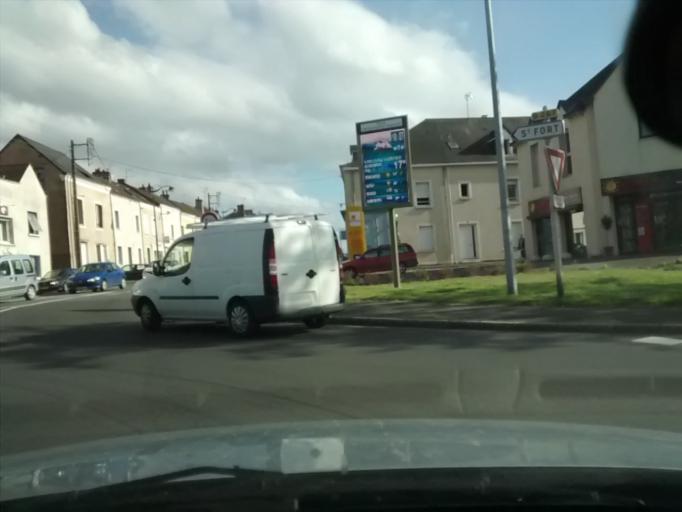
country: FR
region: Pays de la Loire
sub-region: Departement de la Mayenne
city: Chateau-Gontier
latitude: 47.8232
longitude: -0.7081
